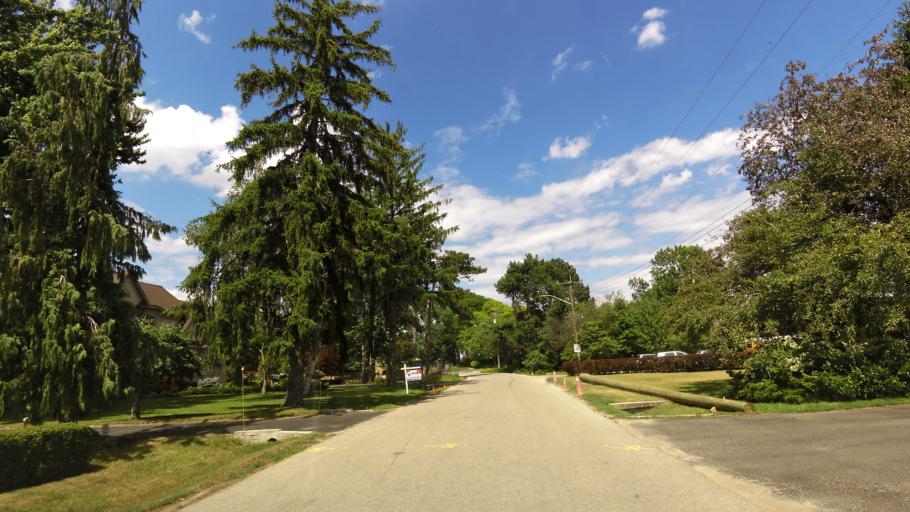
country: CA
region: Ontario
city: Mississauga
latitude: 43.5093
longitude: -79.6025
